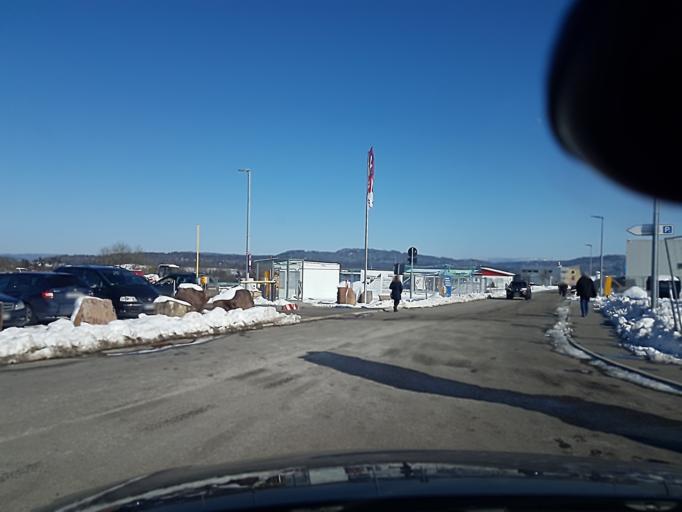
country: DE
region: Baden-Wuerttemberg
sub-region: Freiburg Region
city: Rottweil
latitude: 48.1797
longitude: 8.6259
